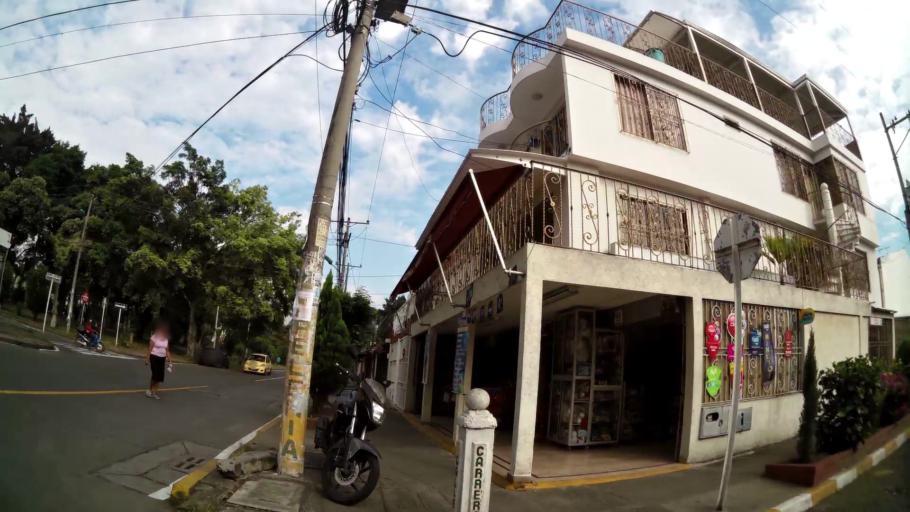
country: CO
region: Valle del Cauca
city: Cali
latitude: 3.4803
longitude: -76.4921
